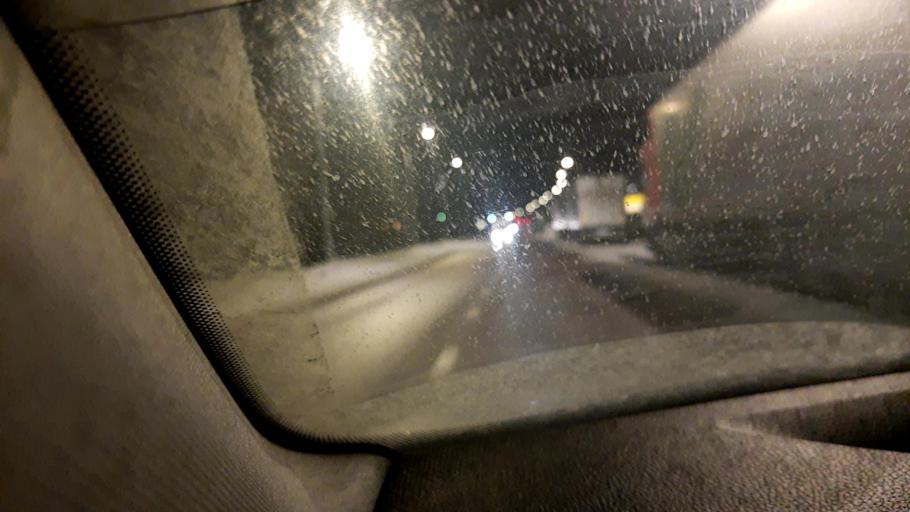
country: RU
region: Moskovskaya
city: Peresvet
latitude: 56.4454
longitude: 38.0986
